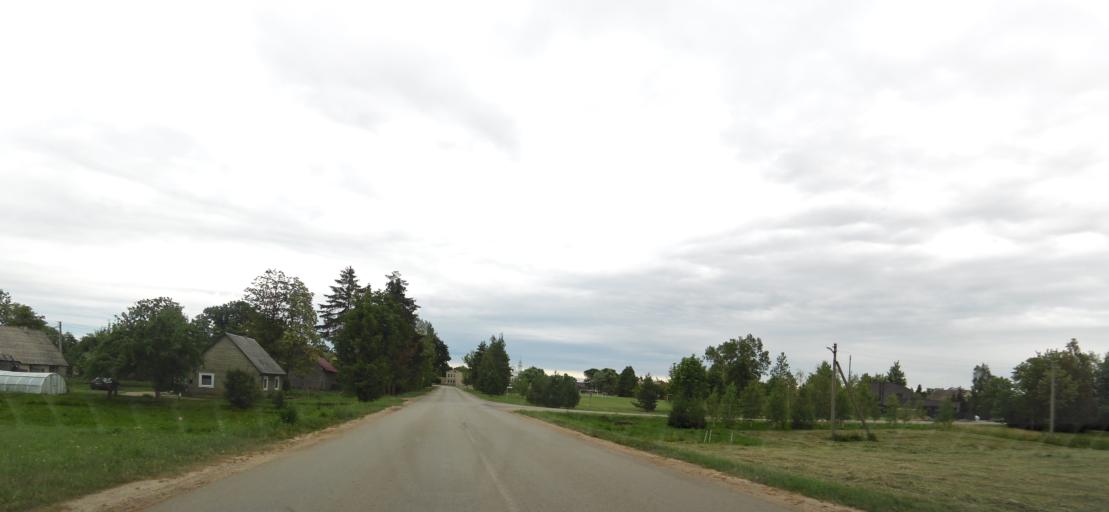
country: LT
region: Panevezys
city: Pasvalys
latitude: 56.0851
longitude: 24.5191
